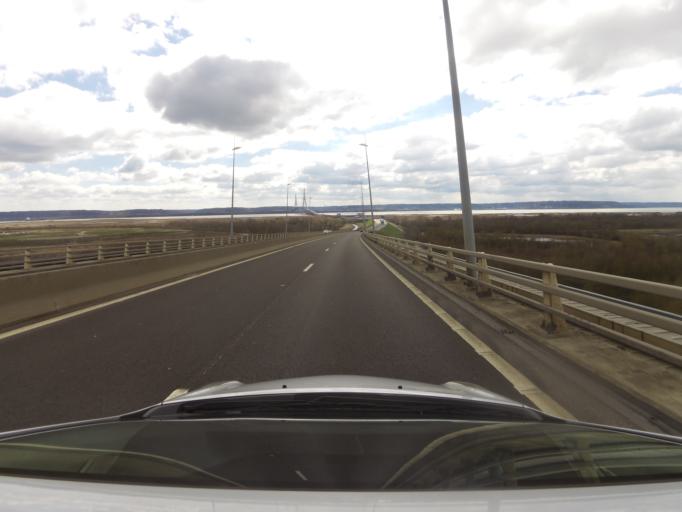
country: FR
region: Haute-Normandie
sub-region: Departement de la Seine-Maritime
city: Rogerville
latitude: 49.4614
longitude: 0.2740
